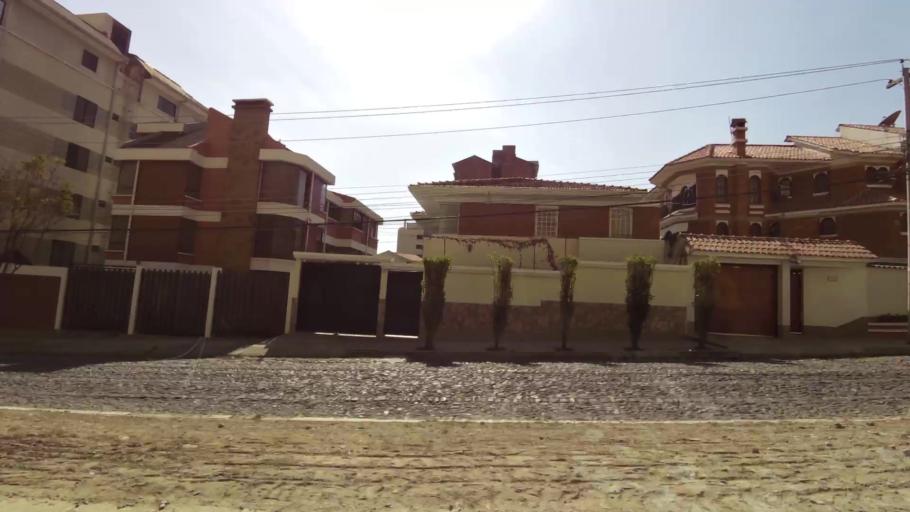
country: BO
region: La Paz
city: La Paz
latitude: -16.5314
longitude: -68.0686
